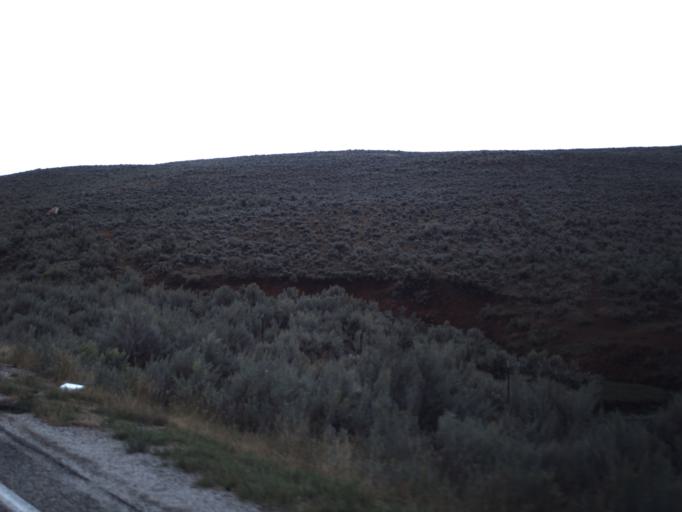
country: US
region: Utah
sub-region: Rich County
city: Randolph
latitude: 41.7876
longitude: -111.2099
